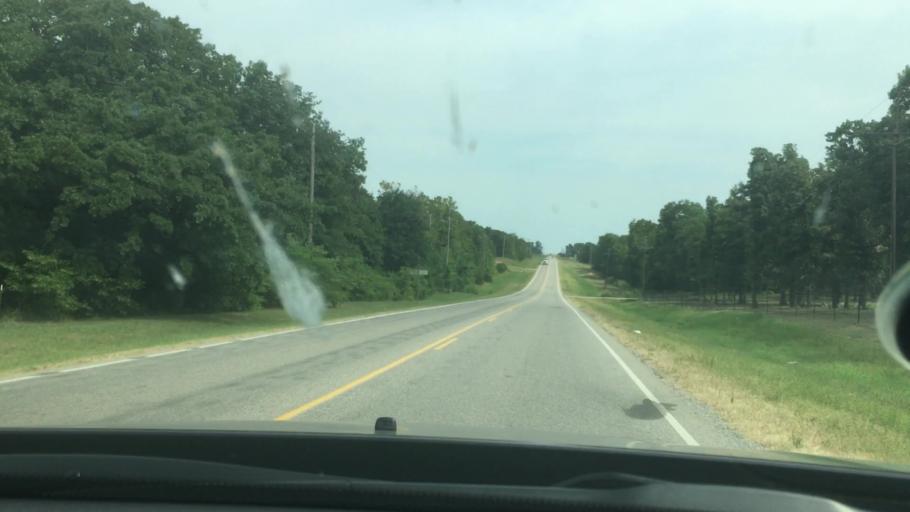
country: US
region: Oklahoma
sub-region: Johnston County
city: Tishomingo
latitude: 34.2592
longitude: -96.4248
